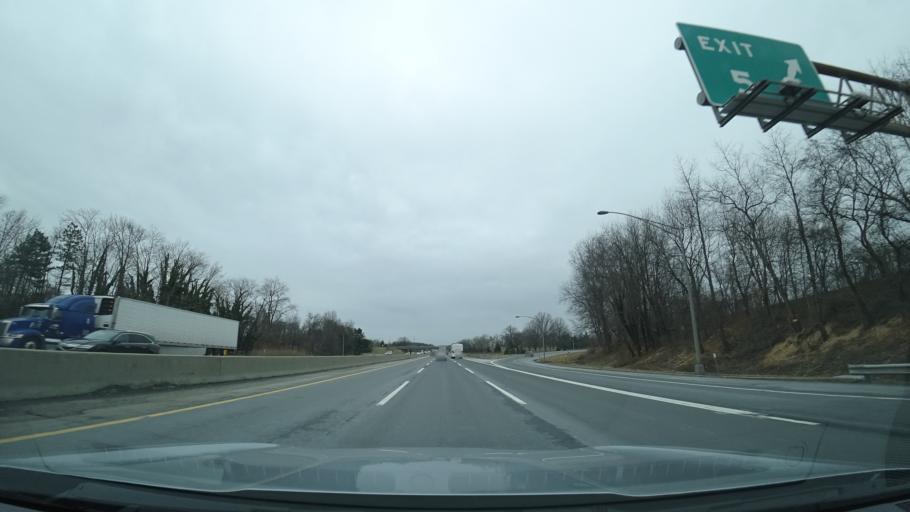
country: US
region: New Jersey
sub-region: Burlington County
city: Mount Holly
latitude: 40.0283
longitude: -74.8200
